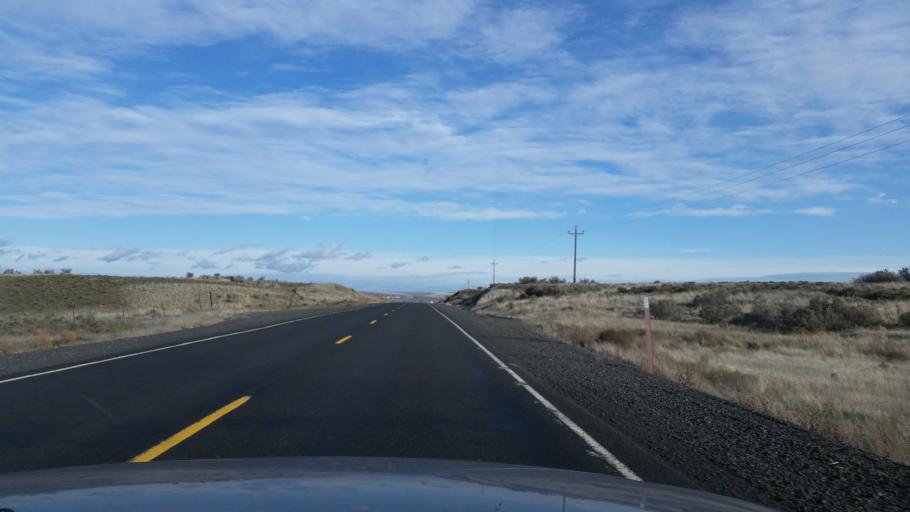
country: US
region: Washington
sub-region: Adams County
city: Ritzville
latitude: 47.3162
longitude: -118.7454
